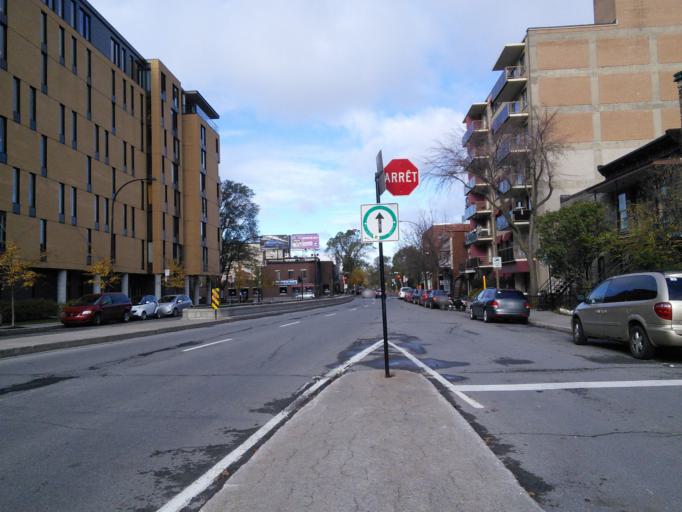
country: CA
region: Quebec
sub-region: Montreal
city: Montreal
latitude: 45.5324
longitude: -73.5955
